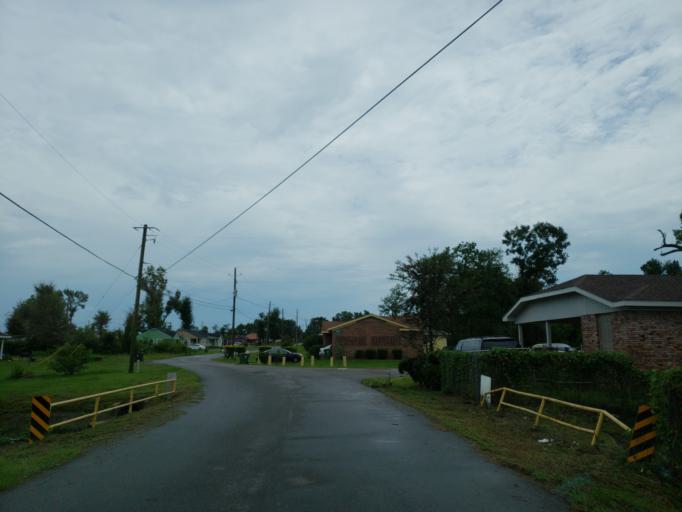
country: US
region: Mississippi
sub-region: Forrest County
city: Hattiesburg
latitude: 31.3106
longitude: -89.2866
